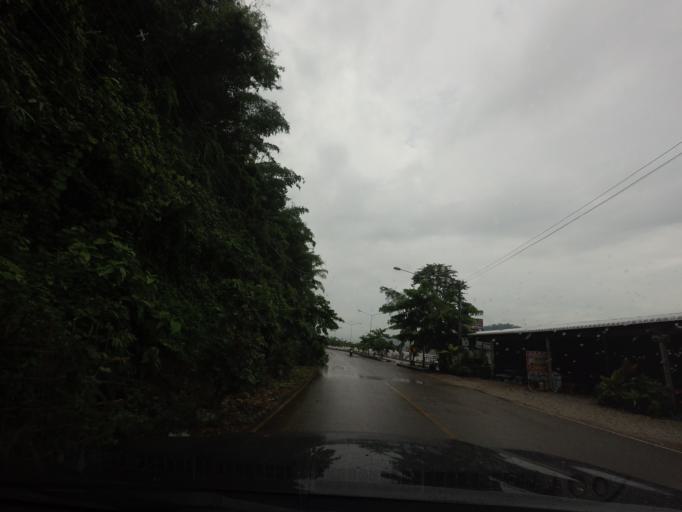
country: TH
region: Nong Khai
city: Sangkhom
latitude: 18.2092
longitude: 102.1369
